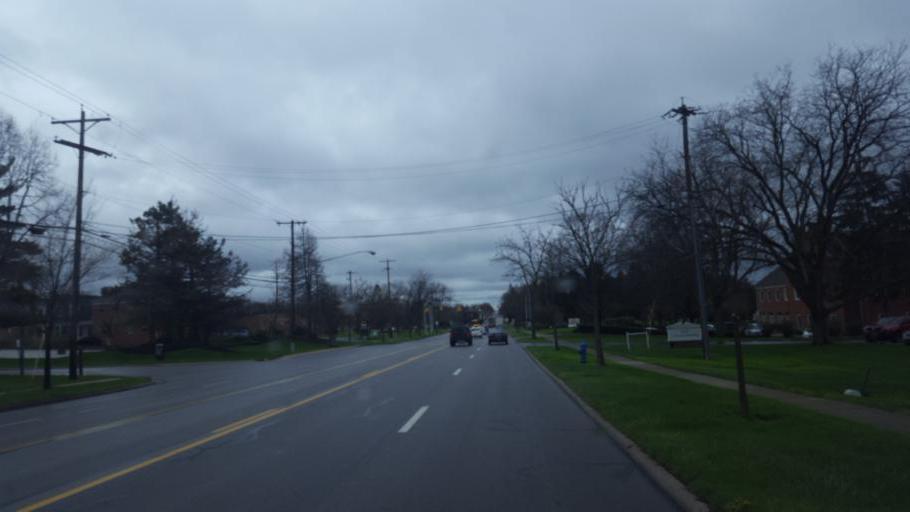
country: US
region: Ohio
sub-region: Franklin County
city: Worthington
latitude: 40.1005
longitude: -83.0174
